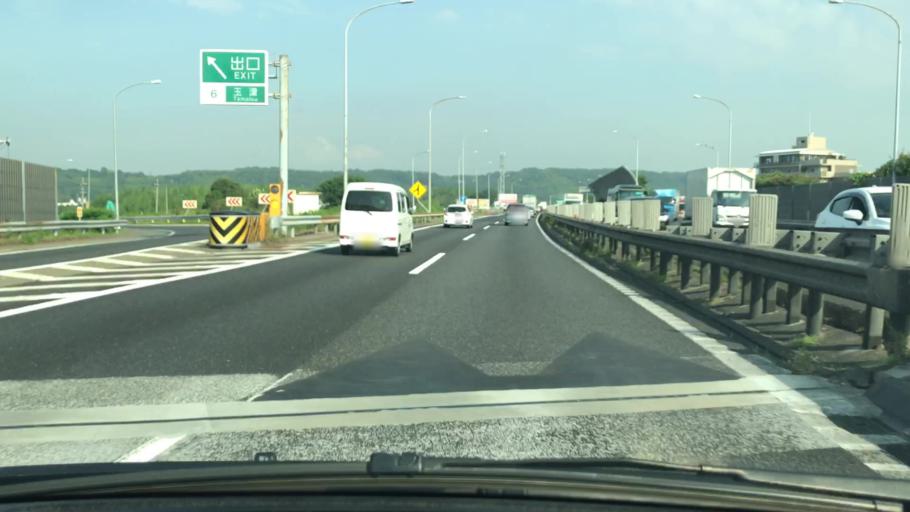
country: JP
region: Hyogo
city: Akashi
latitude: 34.6845
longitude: 134.9811
